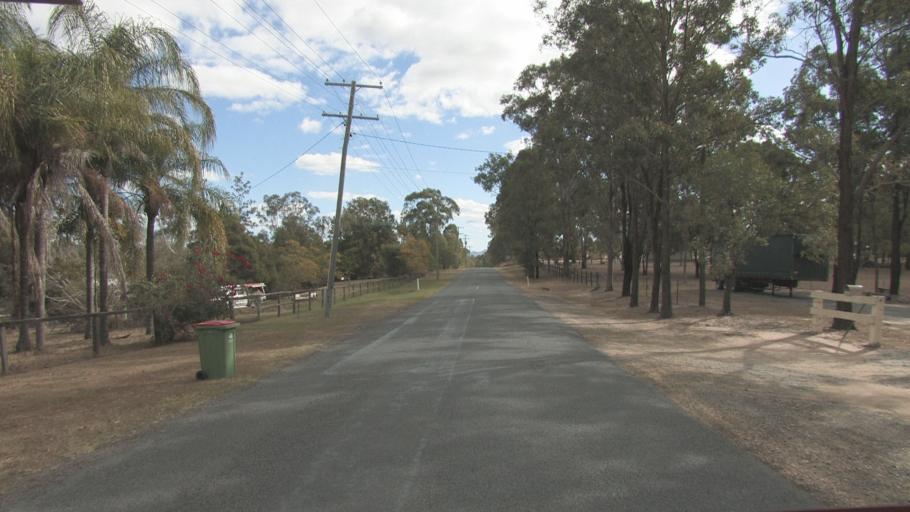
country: AU
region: Queensland
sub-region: Logan
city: Cedar Vale
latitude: -27.8713
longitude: 153.0214
